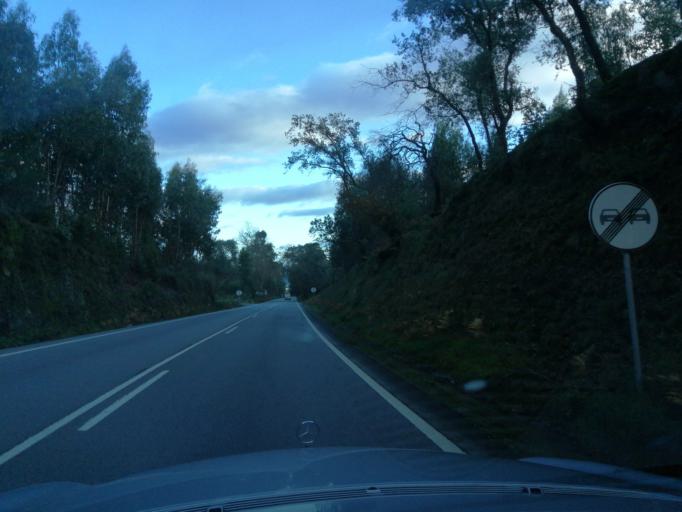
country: PT
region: Braga
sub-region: Barcelos
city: Vila Frescainha
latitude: 41.5686
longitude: -8.6754
